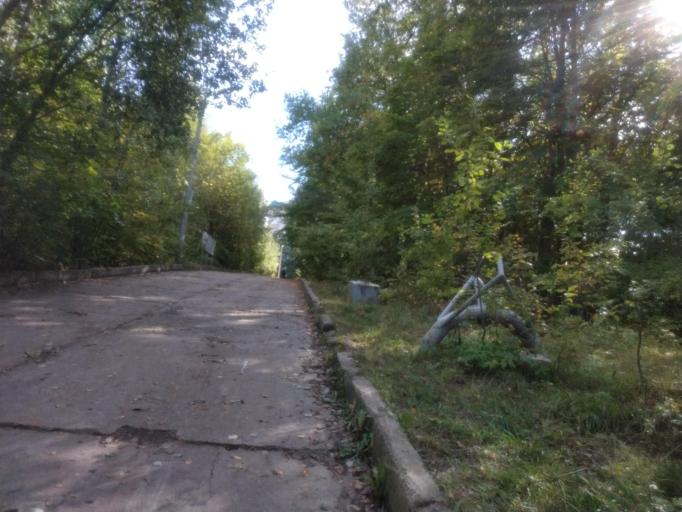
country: RU
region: Chuvashia
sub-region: Cheboksarskiy Rayon
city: Cheboksary
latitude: 56.1536
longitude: 47.1650
